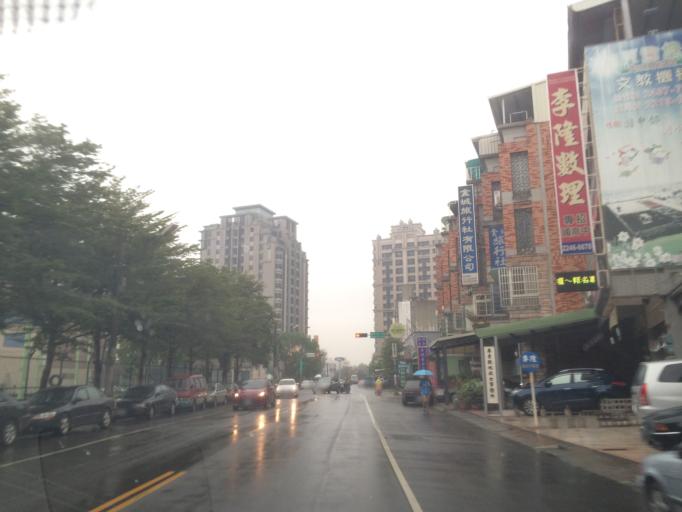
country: TW
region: Taiwan
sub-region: Taichung City
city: Taichung
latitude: 24.1830
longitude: 120.6880
